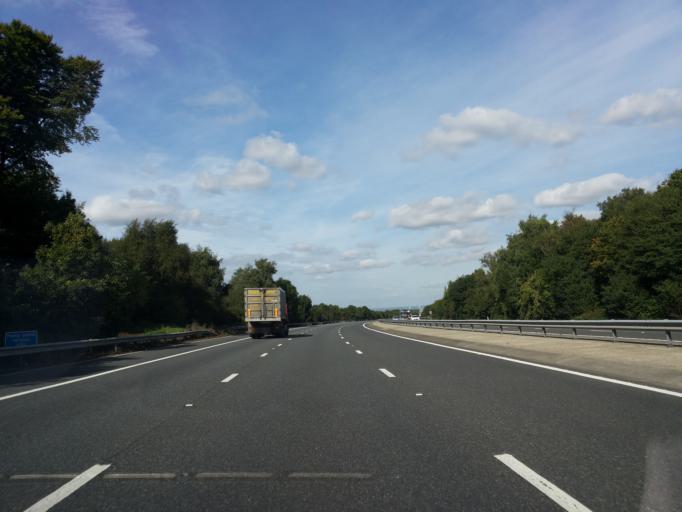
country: GB
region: England
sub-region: Kent
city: Borough Green
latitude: 51.3266
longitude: 0.2741
